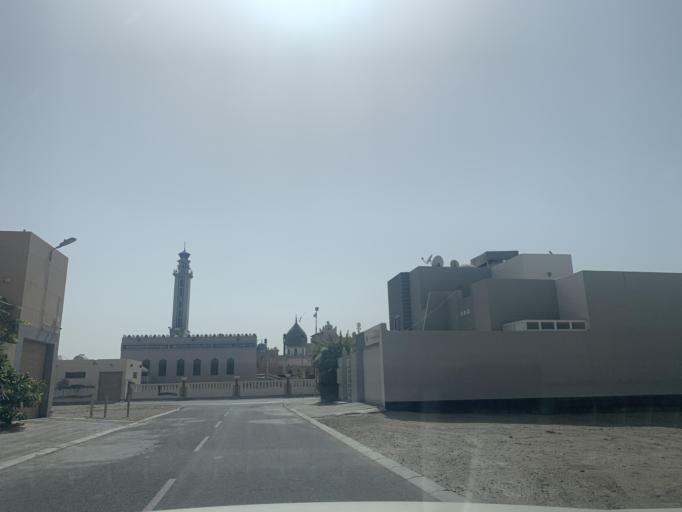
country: BH
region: Northern
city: Sitrah
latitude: 26.1672
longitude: 50.6267
